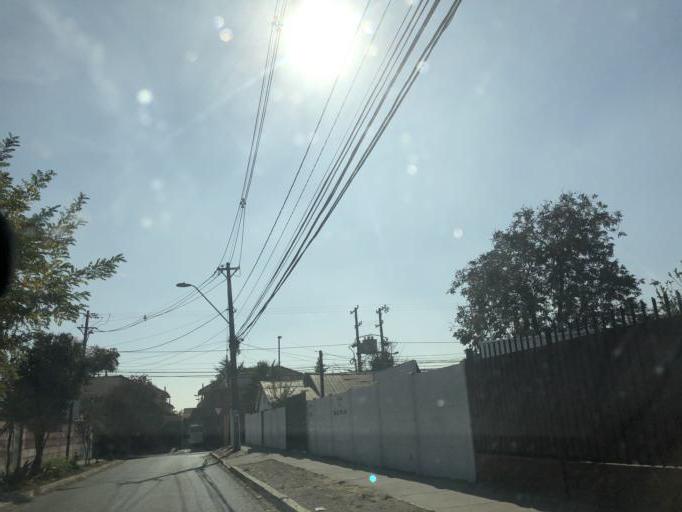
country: CL
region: Santiago Metropolitan
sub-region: Provincia de Cordillera
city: Puente Alto
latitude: -33.6027
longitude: -70.5913
